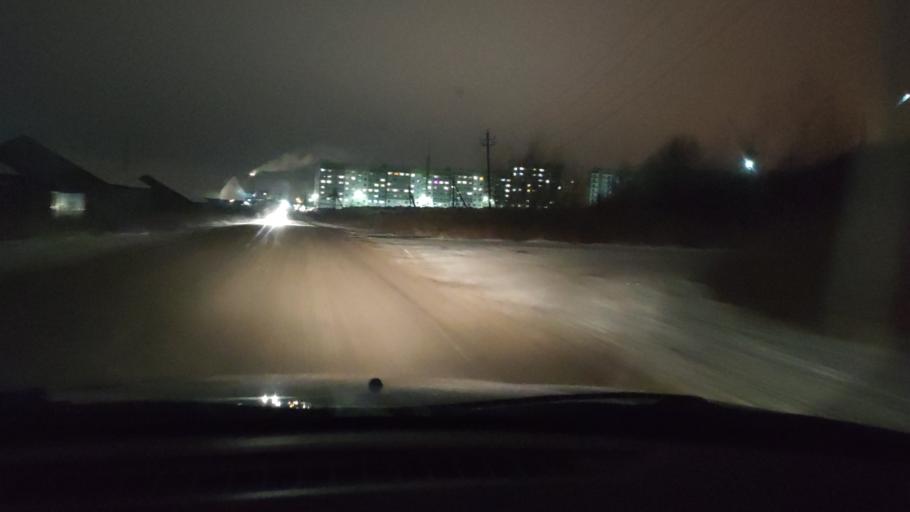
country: RU
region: Perm
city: Froly
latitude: 57.9195
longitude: 56.2910
